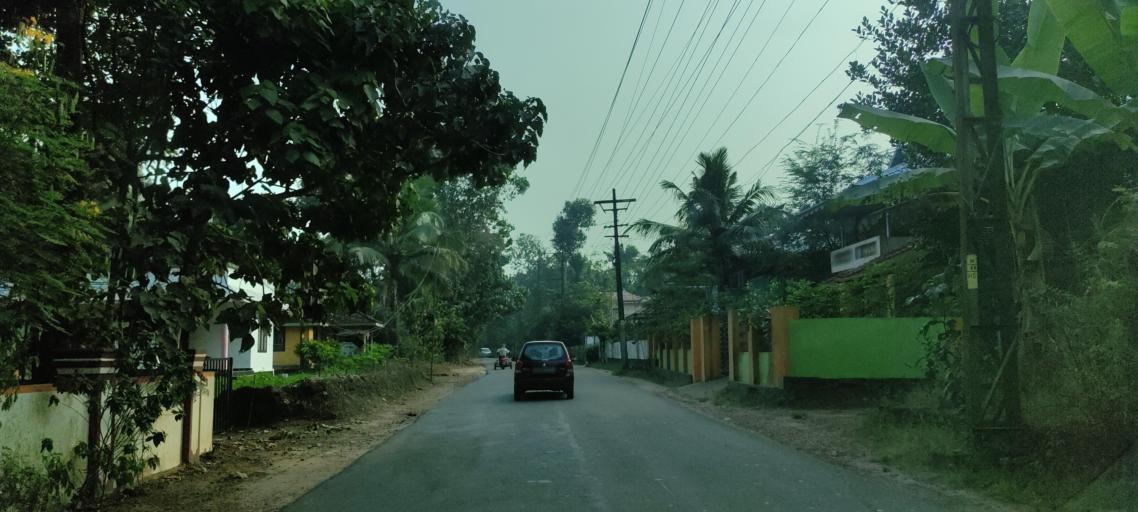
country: IN
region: Kerala
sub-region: Kottayam
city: Vaikam
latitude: 9.7113
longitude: 76.4756
